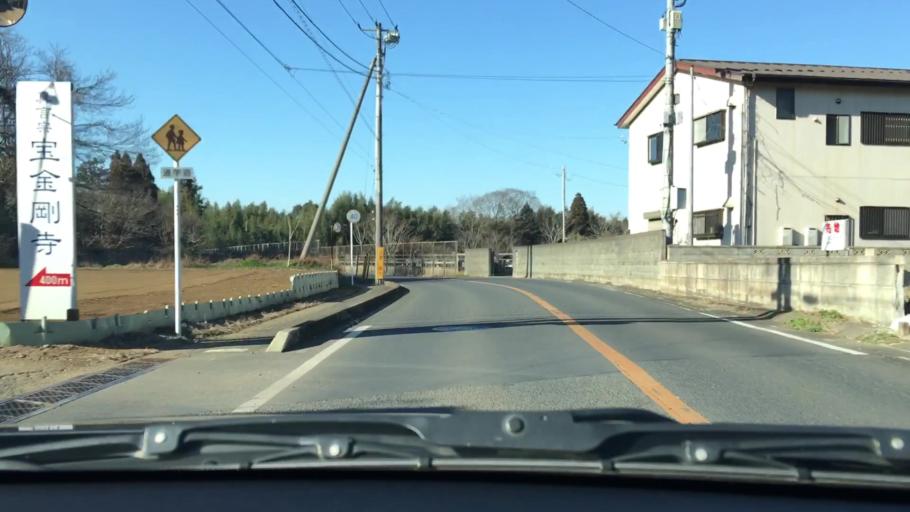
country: JP
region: Chiba
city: Shisui
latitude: 35.6961
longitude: 140.2570
